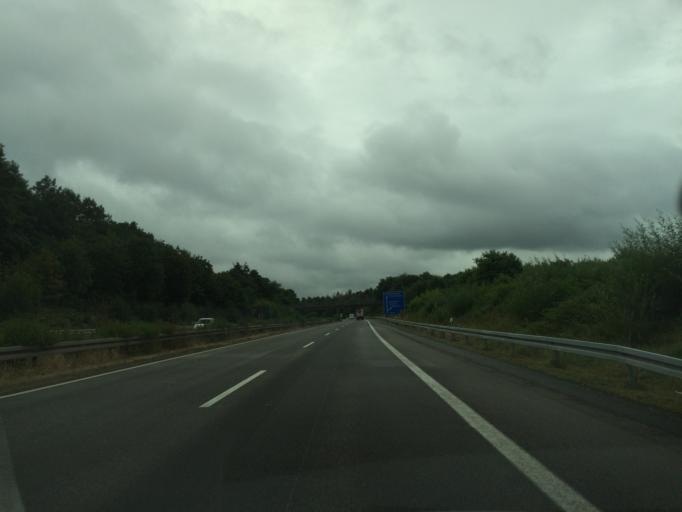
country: DE
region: Saarland
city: Saarwellingen
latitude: 49.3371
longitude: 6.8034
